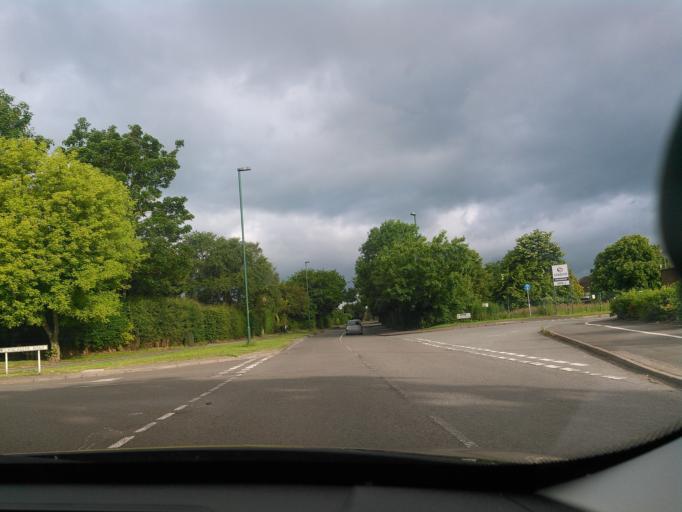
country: GB
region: England
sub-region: Shropshire
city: Shrewsbury
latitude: 52.7387
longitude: -2.7306
